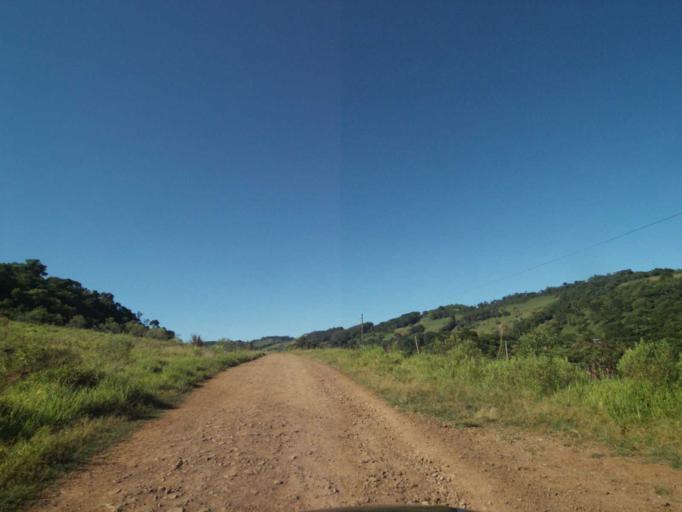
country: BR
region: Parana
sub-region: Francisco Beltrao
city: Francisco Beltrao
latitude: -26.1468
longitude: -53.3125
